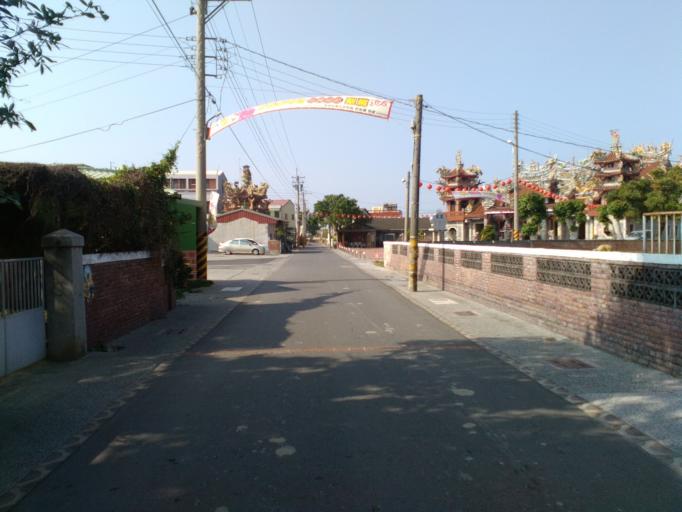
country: TW
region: Taiwan
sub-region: Chiayi
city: Taibao
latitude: 23.5679
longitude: 120.3227
